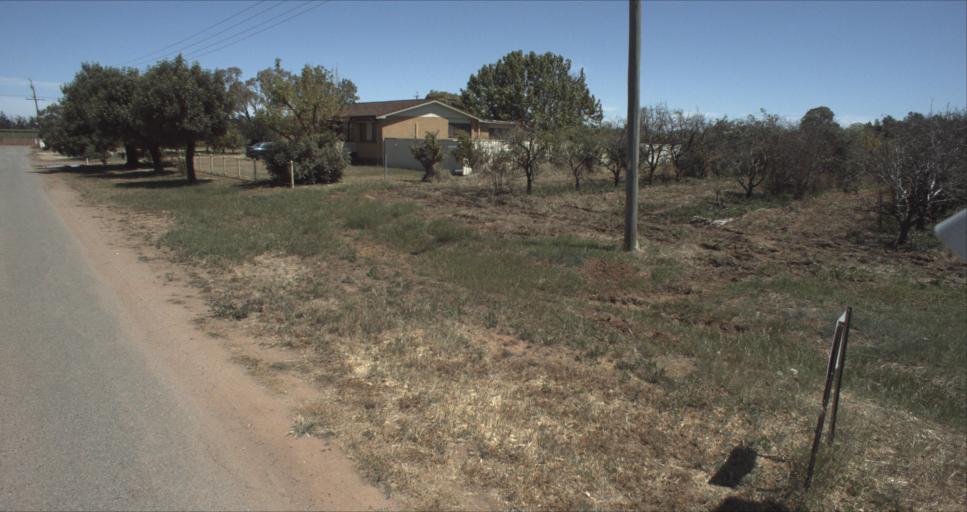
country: AU
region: New South Wales
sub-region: Leeton
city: Leeton
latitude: -34.5301
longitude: 146.3333
